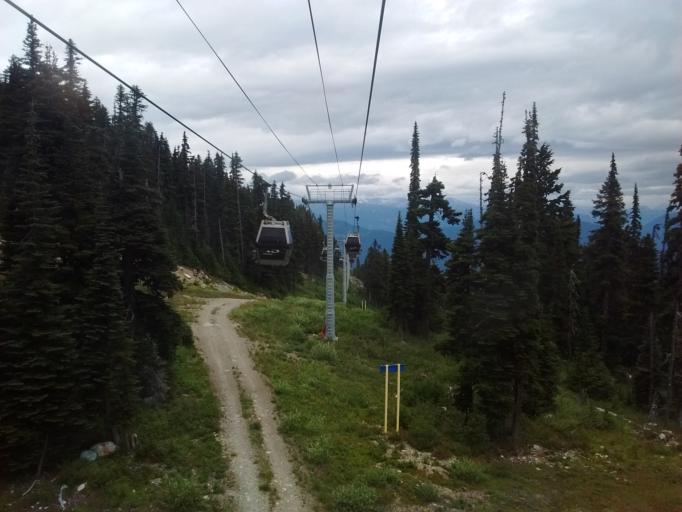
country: CA
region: British Columbia
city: Whistler
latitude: 50.0772
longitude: -122.9482
